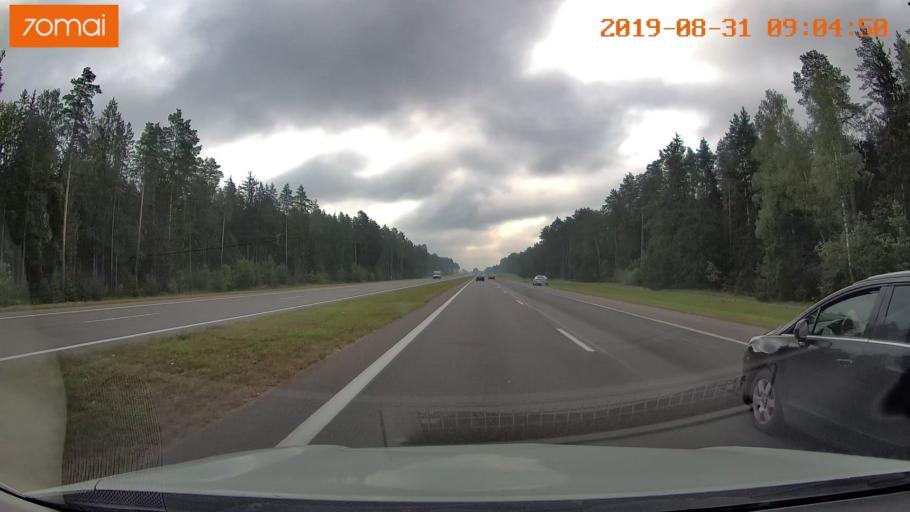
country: BY
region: Minsk
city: Chervyen'
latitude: 53.7299
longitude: 28.3579
